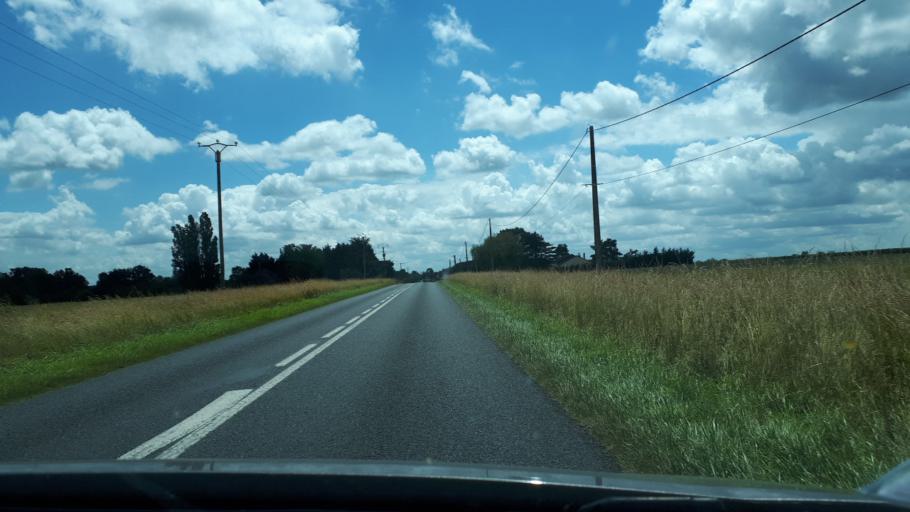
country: FR
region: Centre
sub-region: Departement du Loir-et-Cher
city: Contres
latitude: 47.3759
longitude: 1.4062
